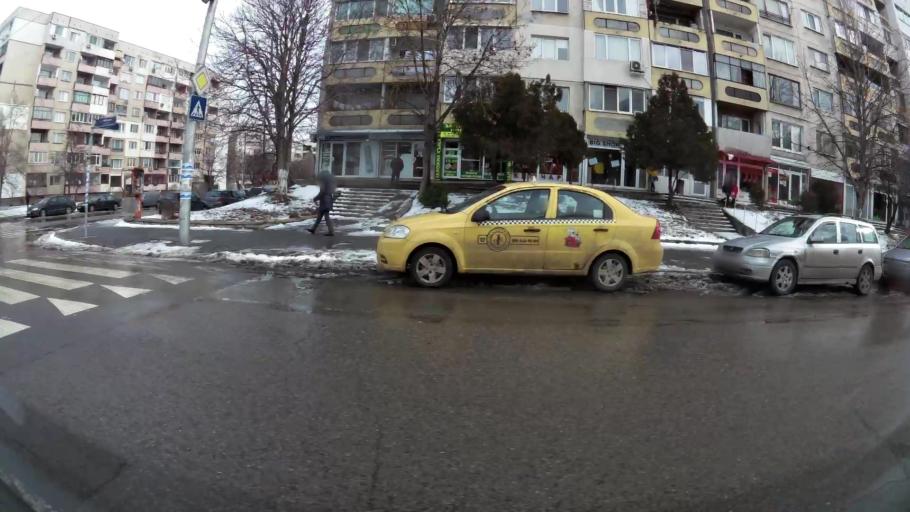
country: BG
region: Sofia-Capital
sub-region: Stolichna Obshtina
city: Sofia
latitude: 42.7082
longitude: 23.3506
